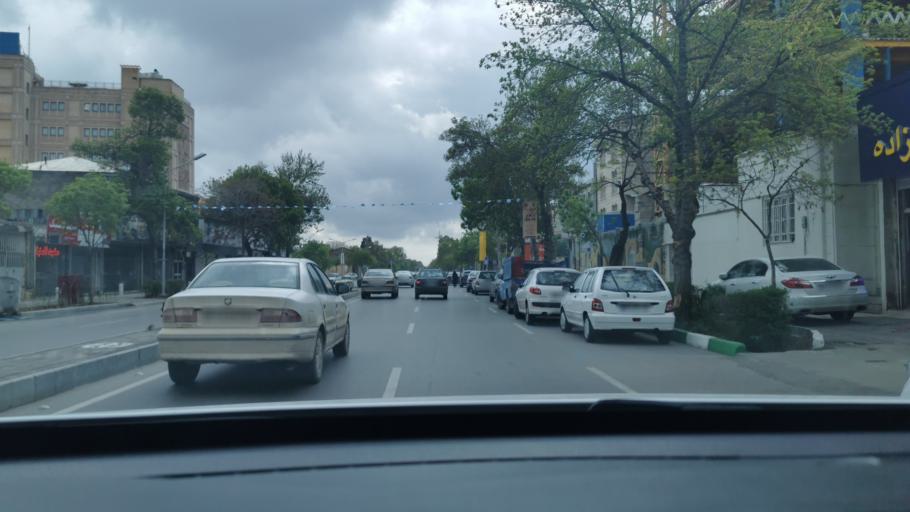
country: IR
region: Razavi Khorasan
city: Mashhad
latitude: 36.2786
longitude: 59.5983
